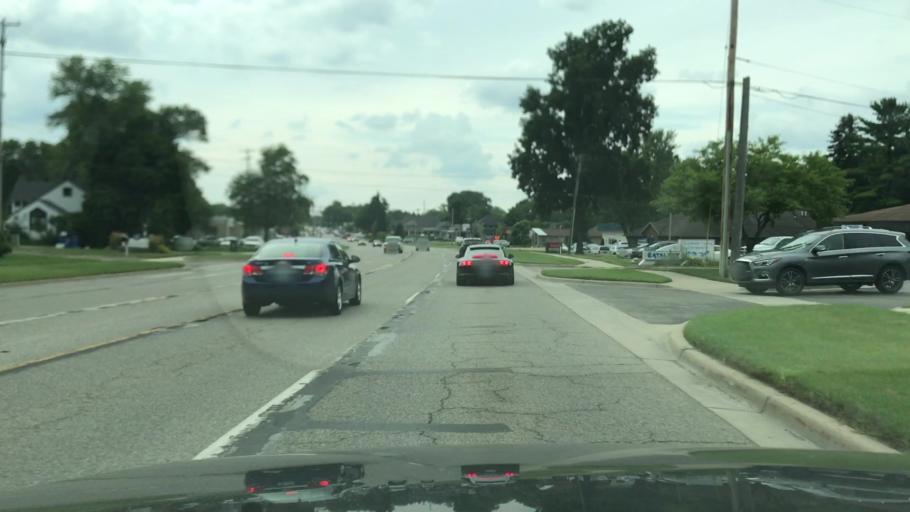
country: US
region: Michigan
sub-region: Kent County
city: East Grand Rapids
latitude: 42.9456
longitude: -85.5494
